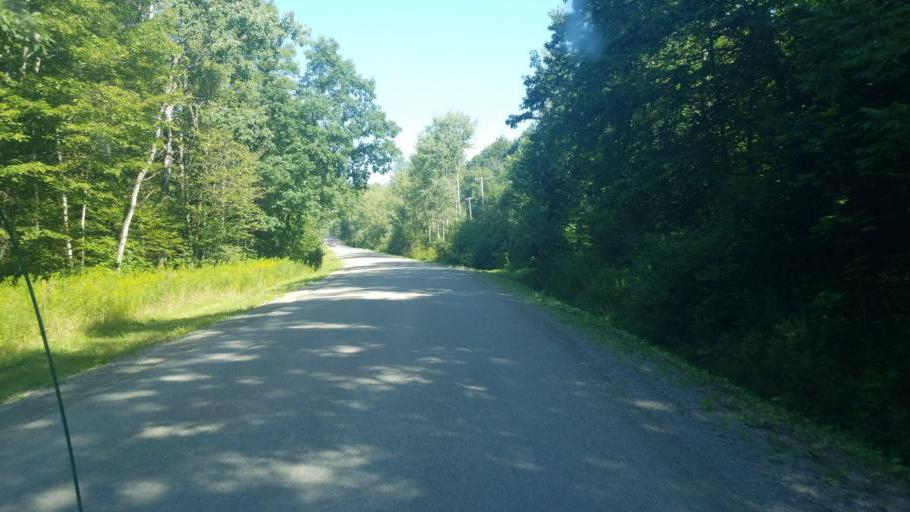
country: US
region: New York
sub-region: Allegany County
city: Wellsville
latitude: 42.0235
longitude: -77.9342
